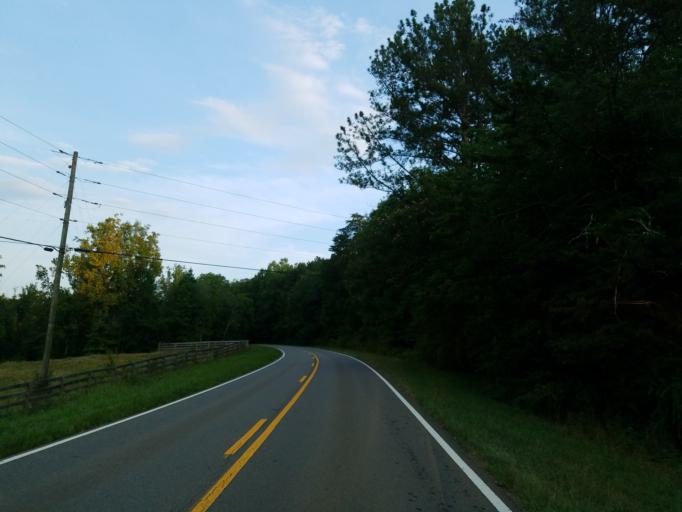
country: US
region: Georgia
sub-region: Pickens County
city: Jasper
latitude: 34.5284
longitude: -84.4773
